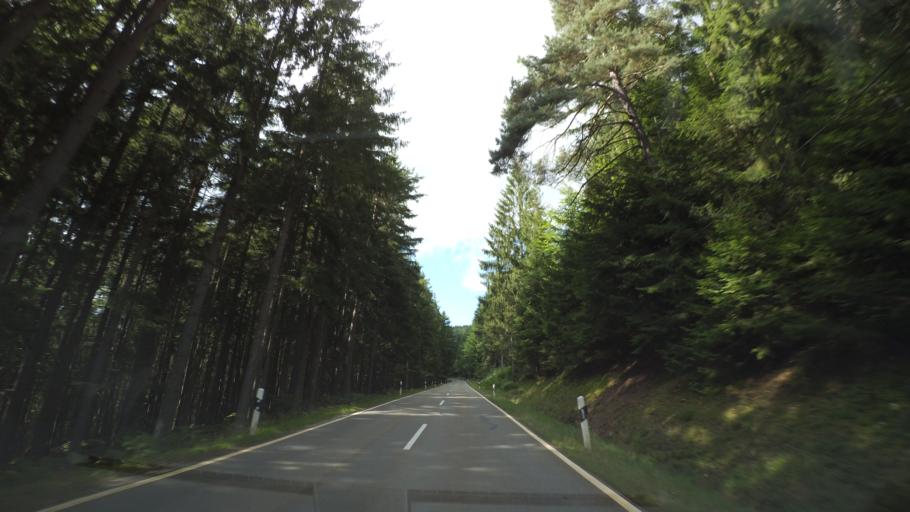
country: DE
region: Bavaria
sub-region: Lower Bavaria
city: Arnbruck
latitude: 49.1505
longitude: 13.0054
